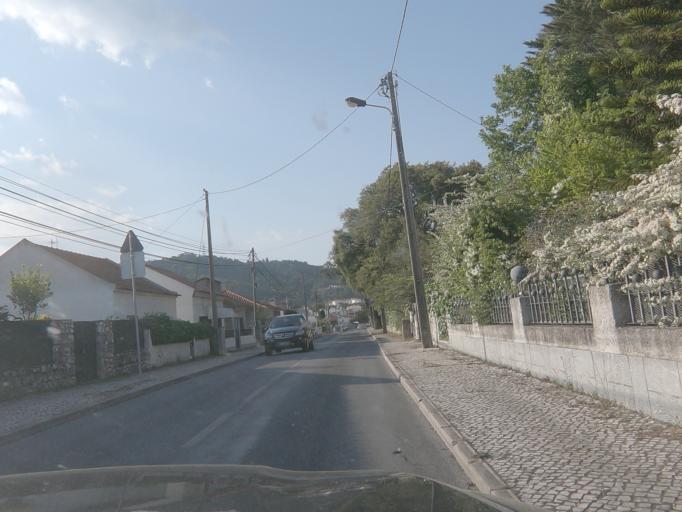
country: PT
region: Setubal
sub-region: Setubal
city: Setubal
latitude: 38.5434
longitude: -8.8984
